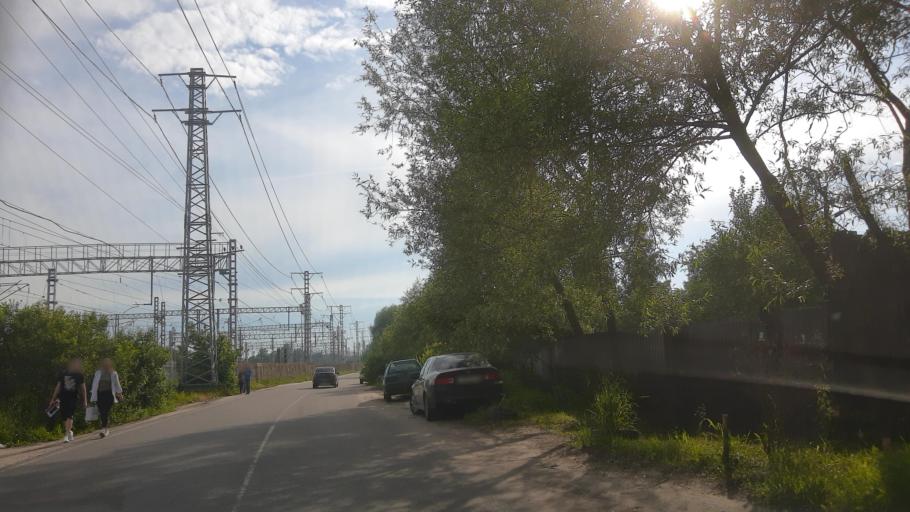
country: RU
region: Moskovskaya
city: Fryazevo
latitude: 55.7324
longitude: 38.4637
